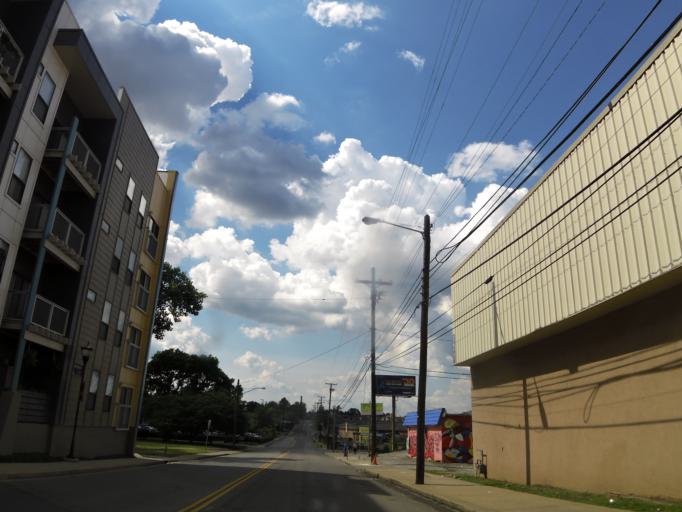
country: US
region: Tennessee
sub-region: Davidson County
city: Nashville
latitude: 36.1570
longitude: -86.7968
